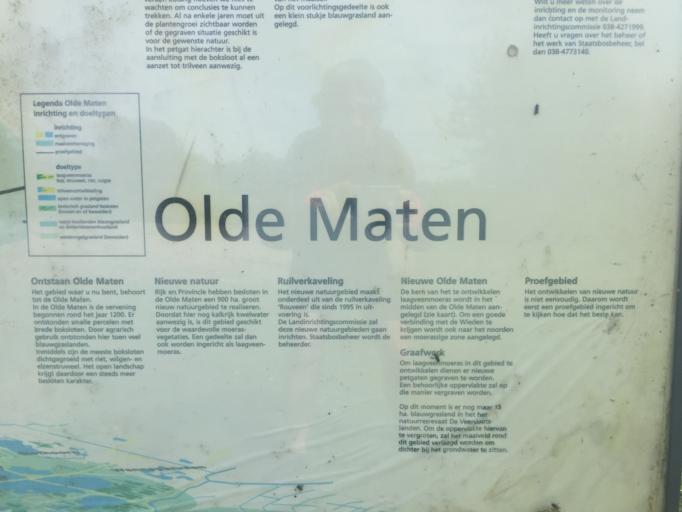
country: NL
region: Overijssel
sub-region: Gemeente Zwartewaterland
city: Hasselt
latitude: 52.6189
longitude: 6.1082
